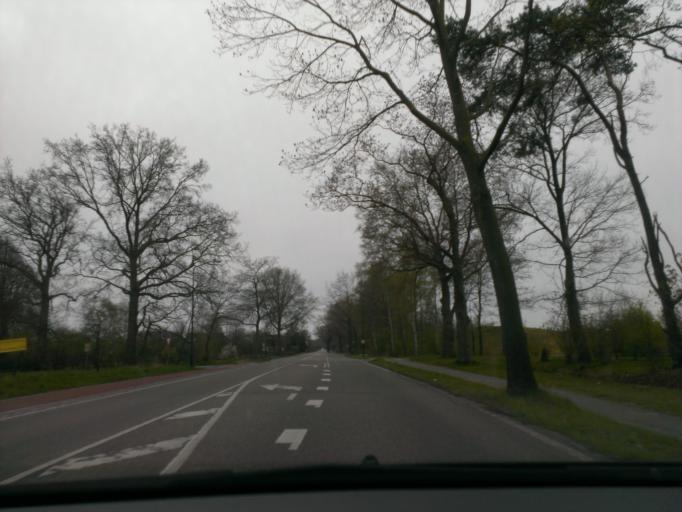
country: NL
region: Gelderland
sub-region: Gemeente Epe
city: Vaassen
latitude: 52.2702
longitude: 5.9584
